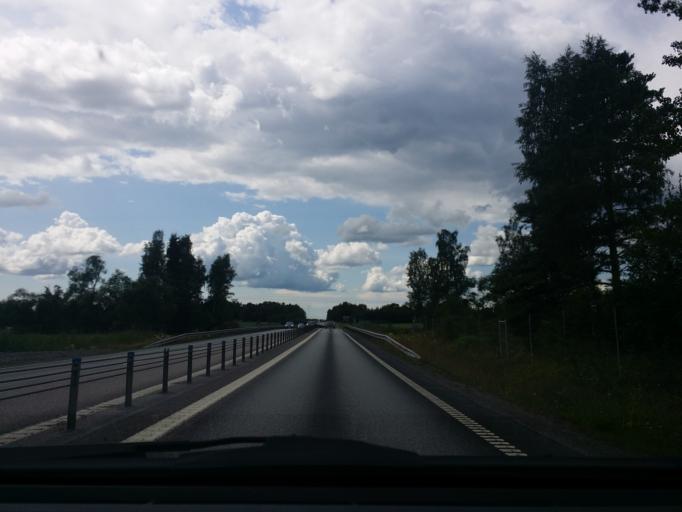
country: SE
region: Vaestmanland
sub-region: Kopings Kommun
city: Koping
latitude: 59.5368
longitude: 15.9947
